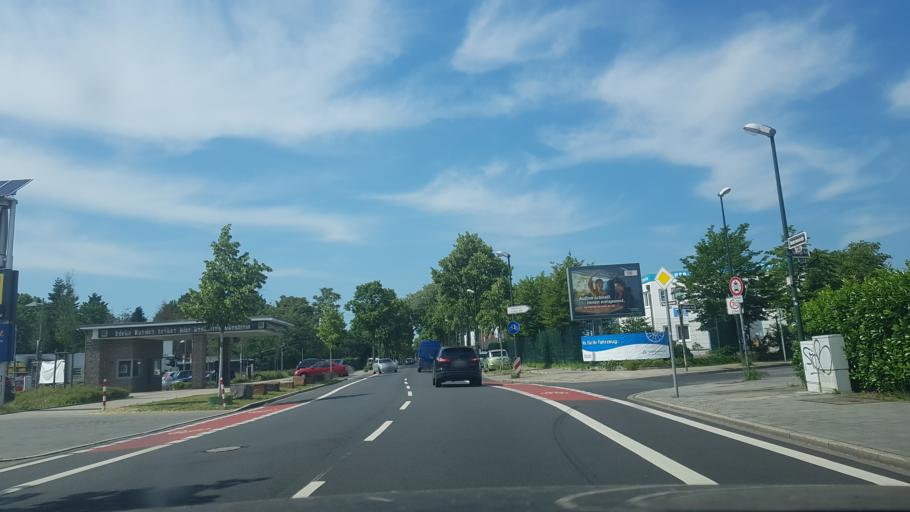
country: DE
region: North Rhine-Westphalia
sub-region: Regierungsbezirk Dusseldorf
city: Dusseldorf
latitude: 51.2745
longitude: 6.7444
